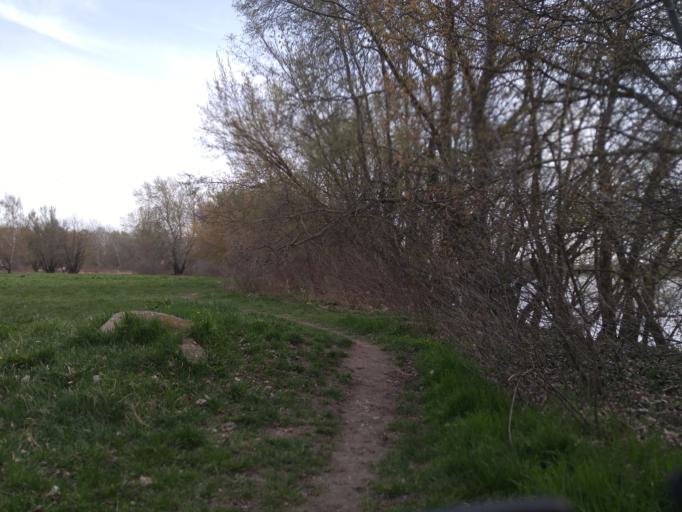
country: HU
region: Pest
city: Vac
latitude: 47.7711
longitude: 19.1285
